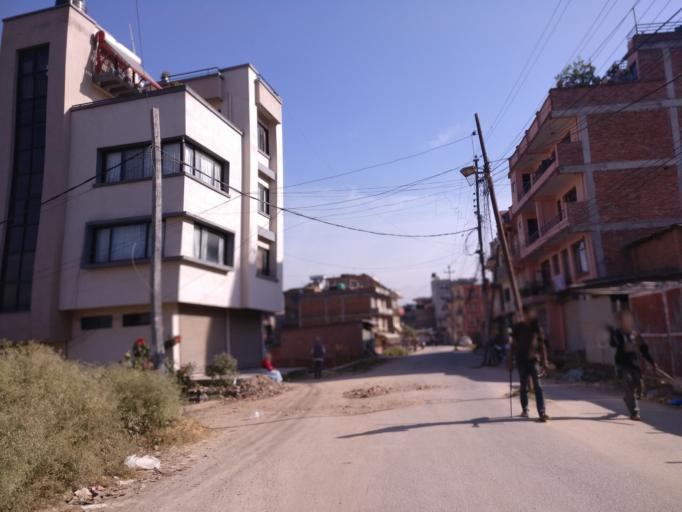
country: NP
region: Central Region
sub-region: Bagmati Zone
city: Patan
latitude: 27.6744
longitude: 85.3334
